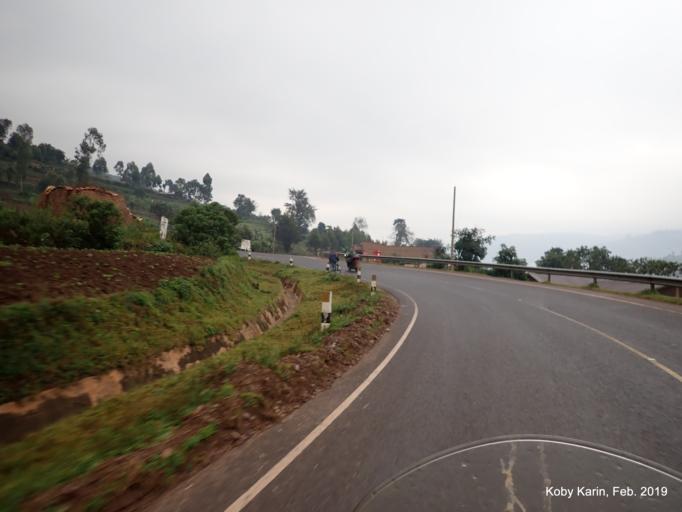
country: UG
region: Western Region
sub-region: Kabale District
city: Kabale
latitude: -1.1371
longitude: 29.9098
